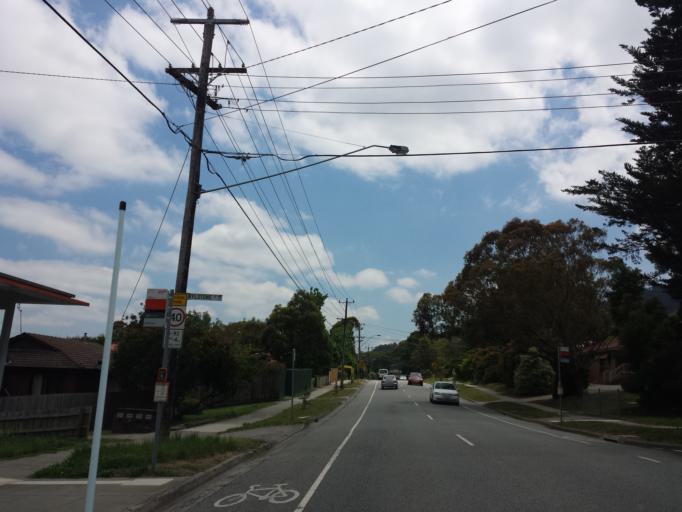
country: AU
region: Victoria
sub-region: Knox
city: Ferntree Gully
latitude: -37.8771
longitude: 145.2993
